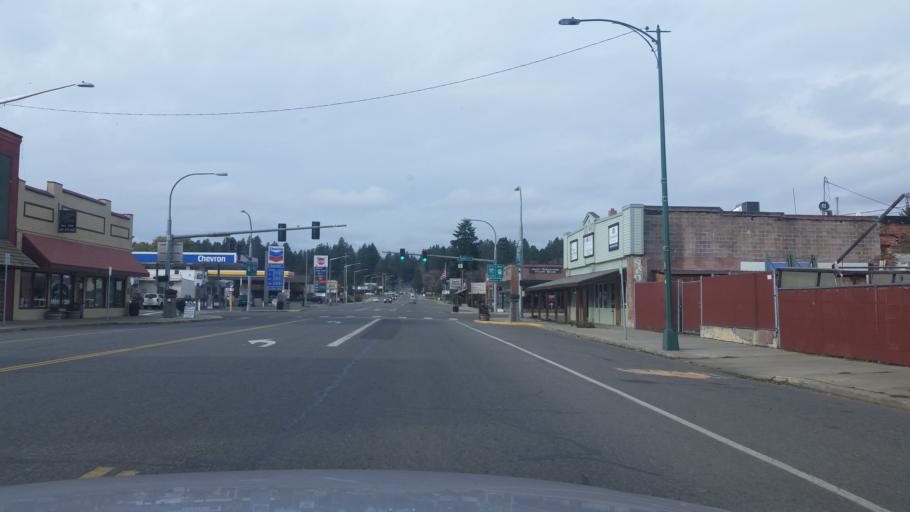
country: US
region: Washington
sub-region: Kittitas County
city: Cle Elum
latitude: 47.1951
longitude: -120.9395
